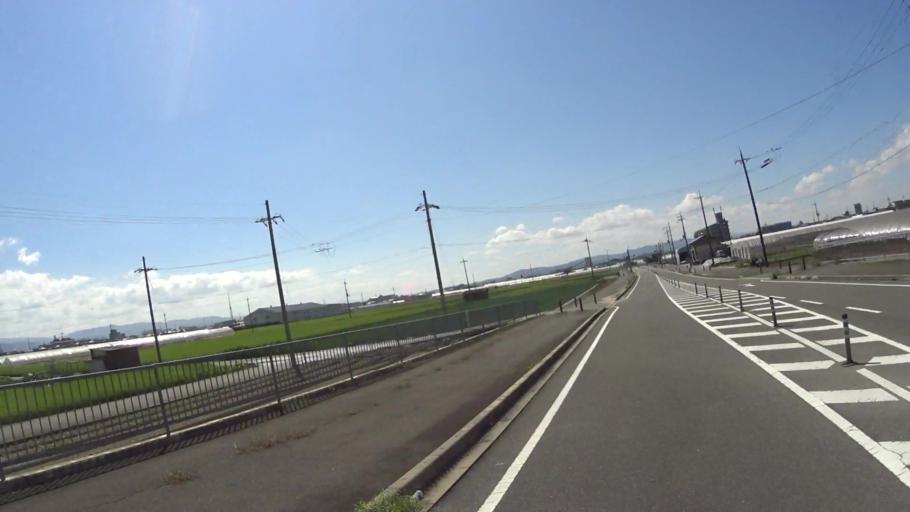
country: JP
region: Kyoto
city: Yawata
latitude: 34.8957
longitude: 135.7246
